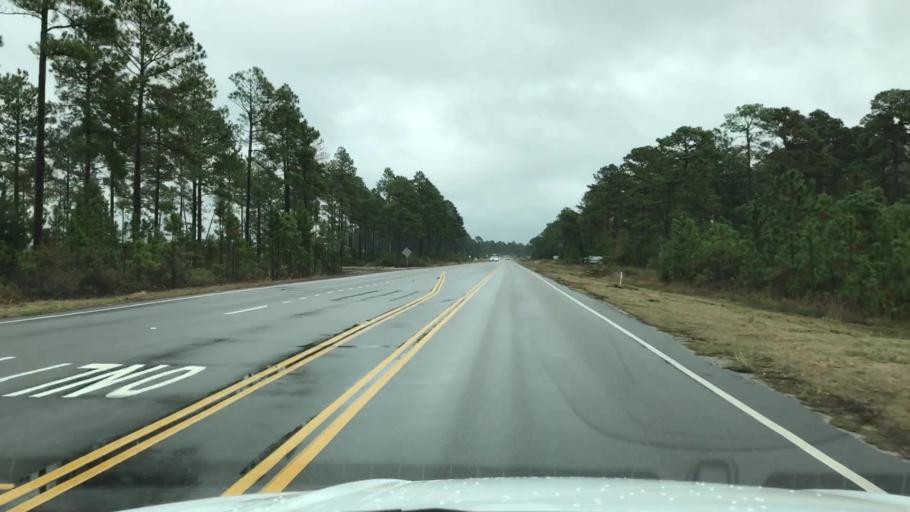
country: US
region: South Carolina
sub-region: Horry County
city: Forestbrook
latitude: 33.7594
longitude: -78.8992
